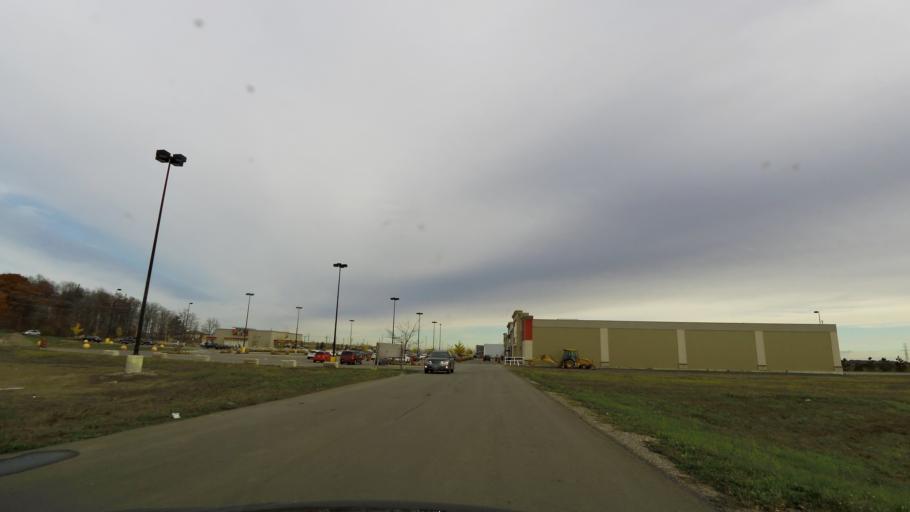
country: CA
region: Ontario
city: Hamilton
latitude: 43.1756
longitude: -79.7920
